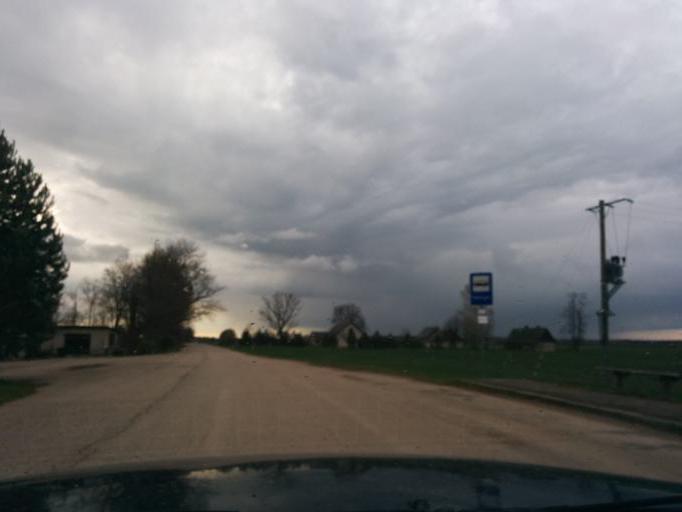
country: LT
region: Siauliu apskritis
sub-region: Joniskis
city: Joniskis
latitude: 56.3736
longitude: 23.5464
